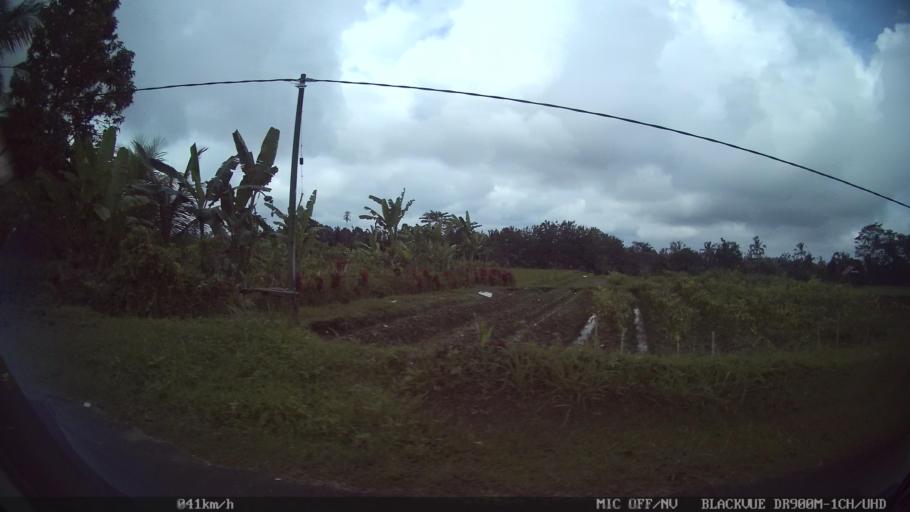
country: ID
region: Bali
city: Badung
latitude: -8.4205
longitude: 115.2274
